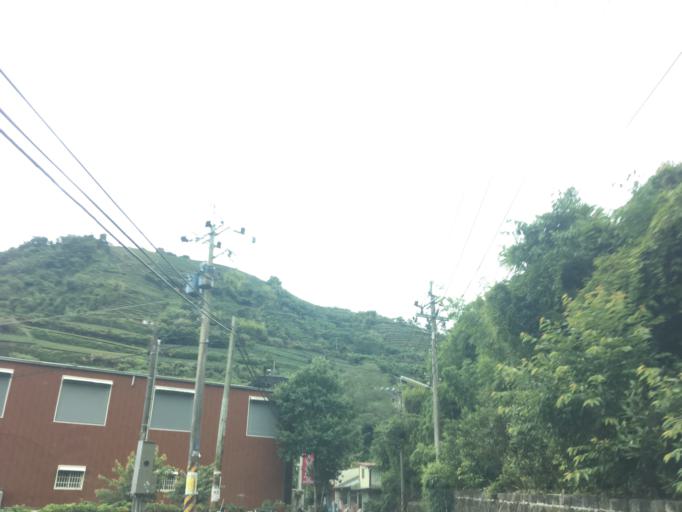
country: TW
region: Taiwan
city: Lugu
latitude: 23.5448
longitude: 120.7059
